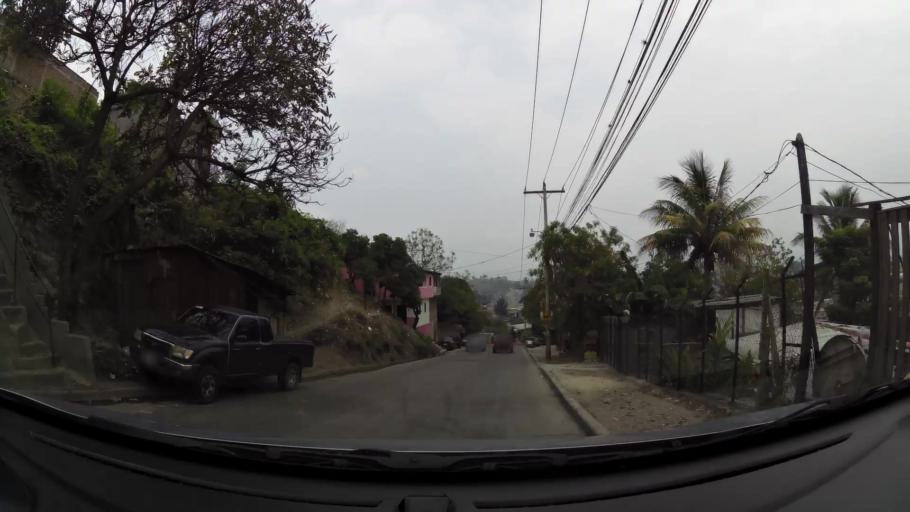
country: HN
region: Francisco Morazan
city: Tegucigalpa
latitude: 14.0738
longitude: -87.2324
